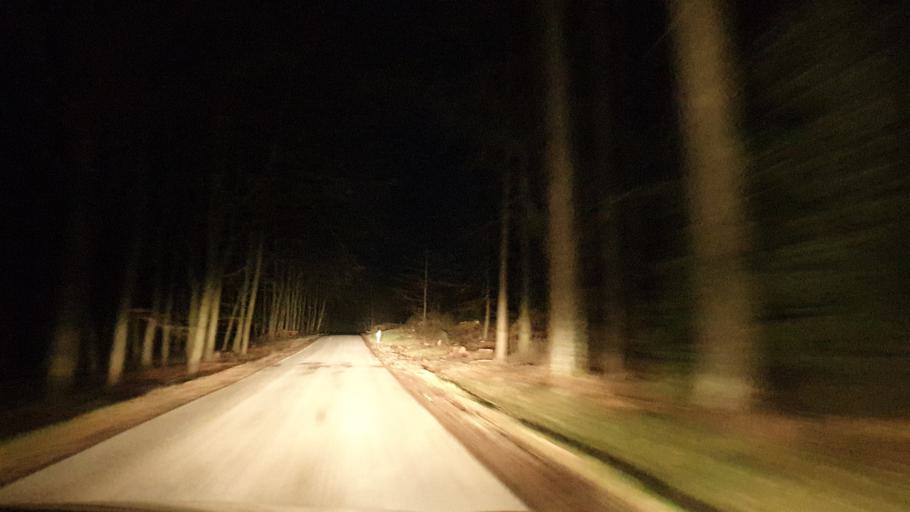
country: DE
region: Rheinland-Pfalz
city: Ratzert
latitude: 50.6437
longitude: 7.6355
